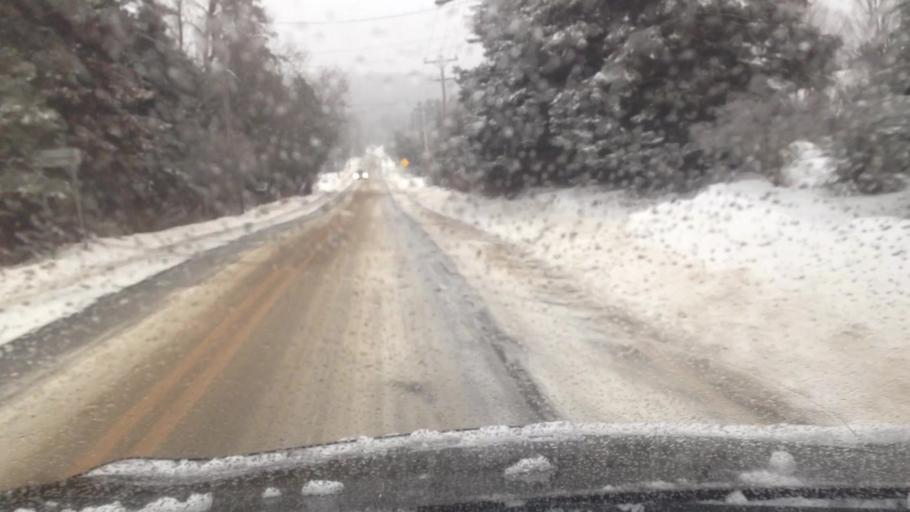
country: CA
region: Quebec
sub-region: Laurentides
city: Mont-Tremblant
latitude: 45.9820
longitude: -74.6123
